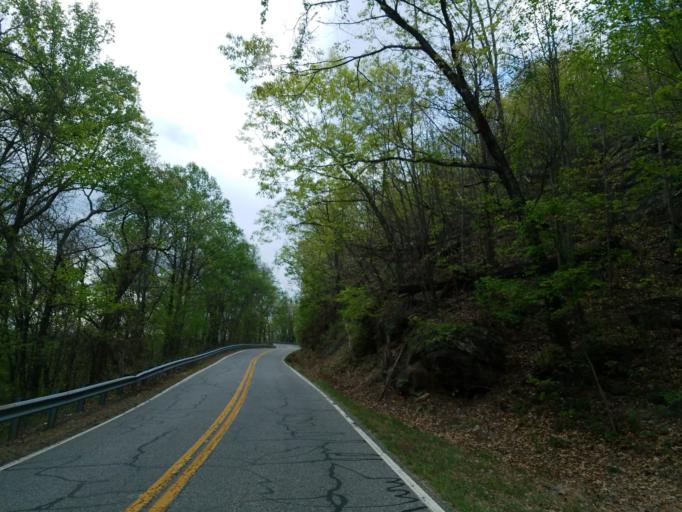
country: US
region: Georgia
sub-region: Lumpkin County
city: Dahlonega
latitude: 34.6430
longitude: -83.9614
